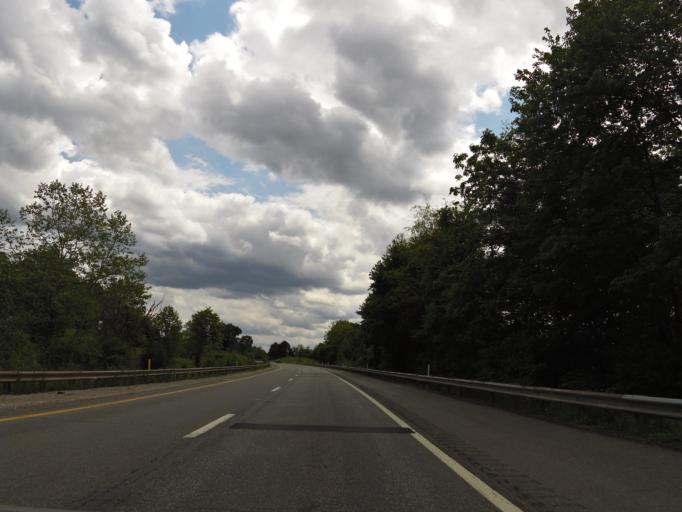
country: US
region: West Virginia
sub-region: Jackson County
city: Ripley
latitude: 38.7509
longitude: -81.6839
